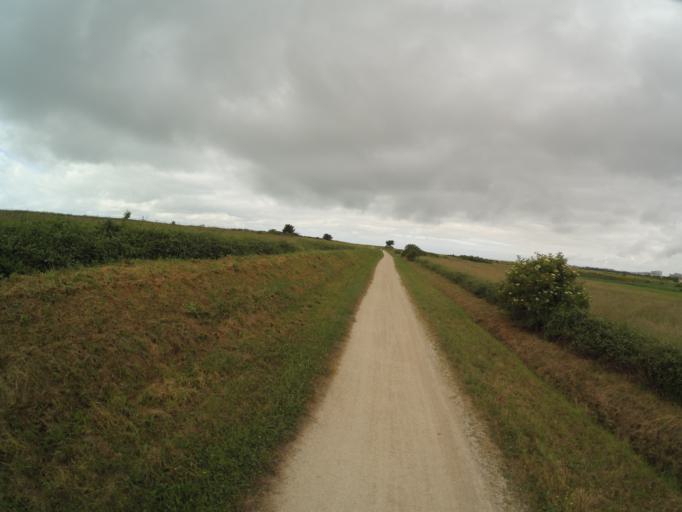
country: FR
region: Poitou-Charentes
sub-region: Departement de la Charente-Maritime
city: Aytre
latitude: 46.1313
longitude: -1.1433
